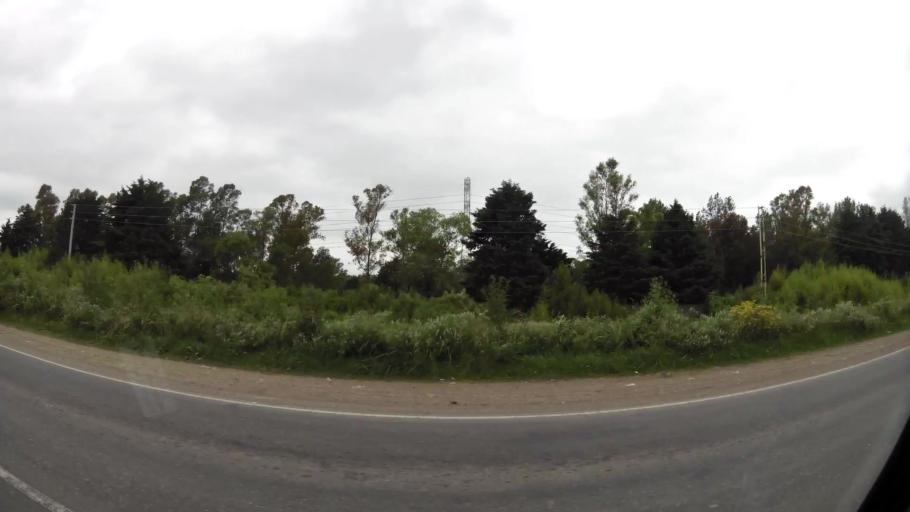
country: AR
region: Buenos Aires
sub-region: Partido de Ezeiza
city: Ezeiza
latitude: -34.8930
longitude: -58.5073
